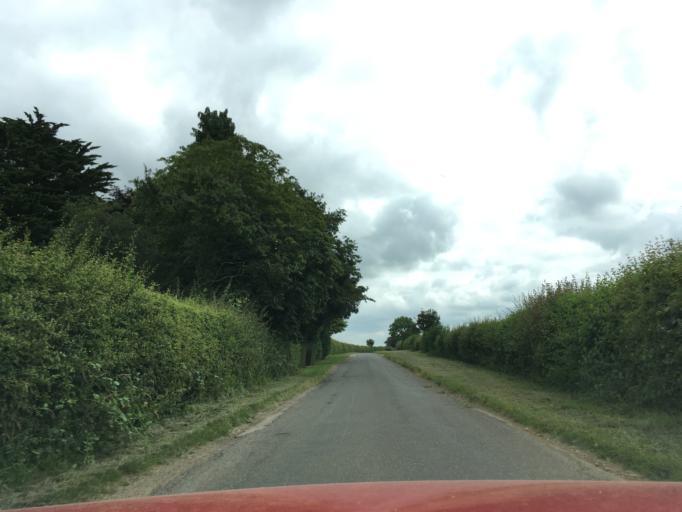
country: GB
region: England
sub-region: Oxfordshire
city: Chipping Norton
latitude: 51.9214
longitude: -1.5253
